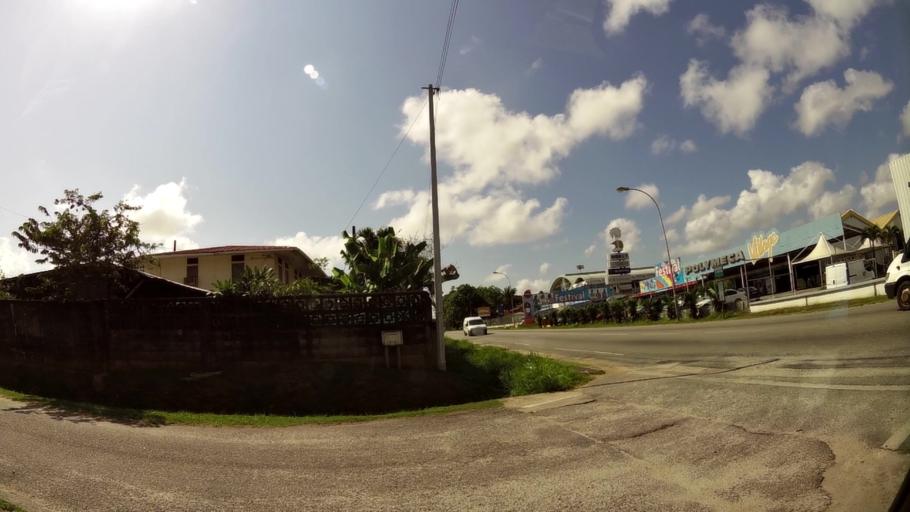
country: GF
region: Guyane
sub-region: Guyane
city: Cayenne
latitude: 4.9363
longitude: -52.3140
